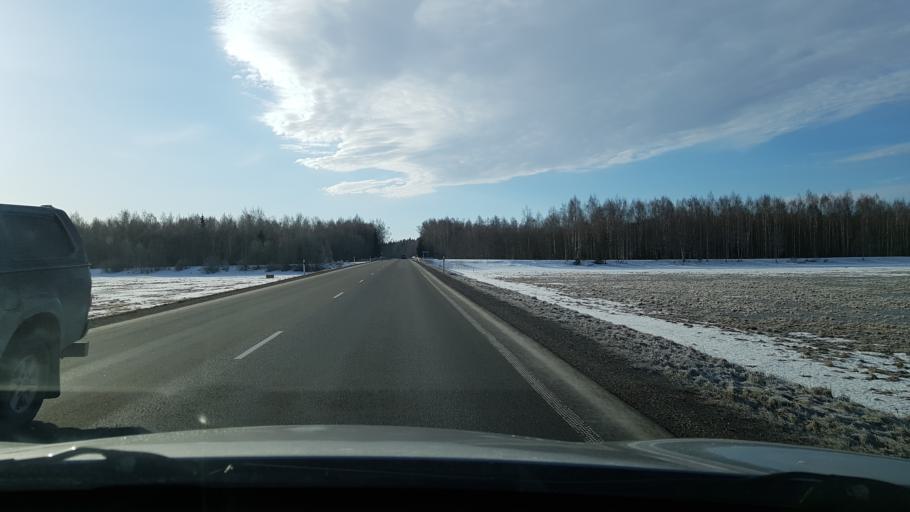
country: EE
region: Viljandimaa
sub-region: Vohma linn
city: Vohma
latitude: 58.5861
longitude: 25.5706
